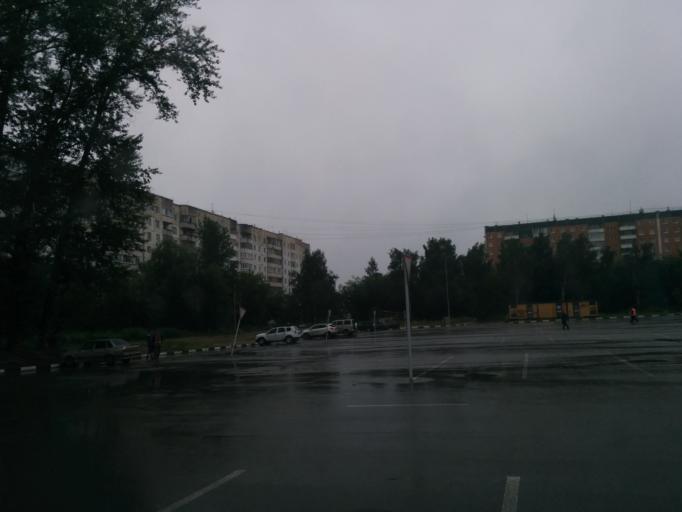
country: RU
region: Perm
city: Kondratovo
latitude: 58.0386
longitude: 56.0335
